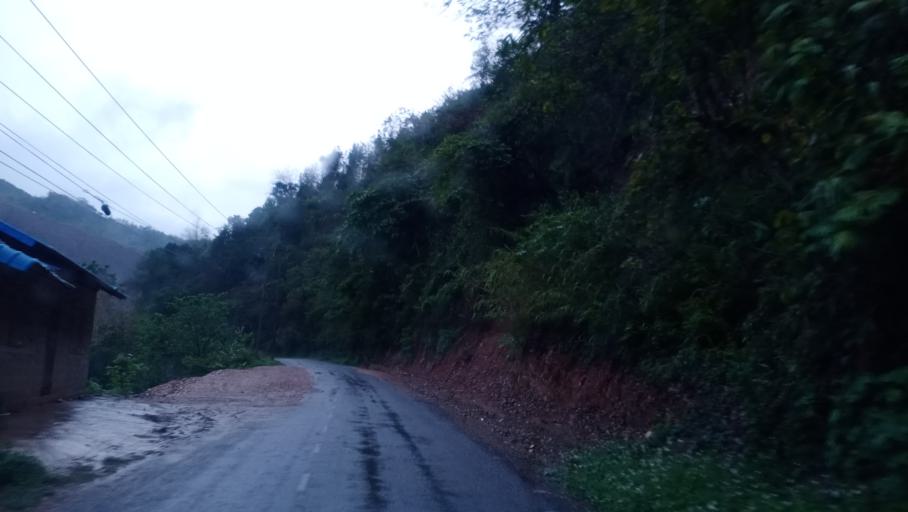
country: LA
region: Phongsali
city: Khoa
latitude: 21.0654
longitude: 102.4858
